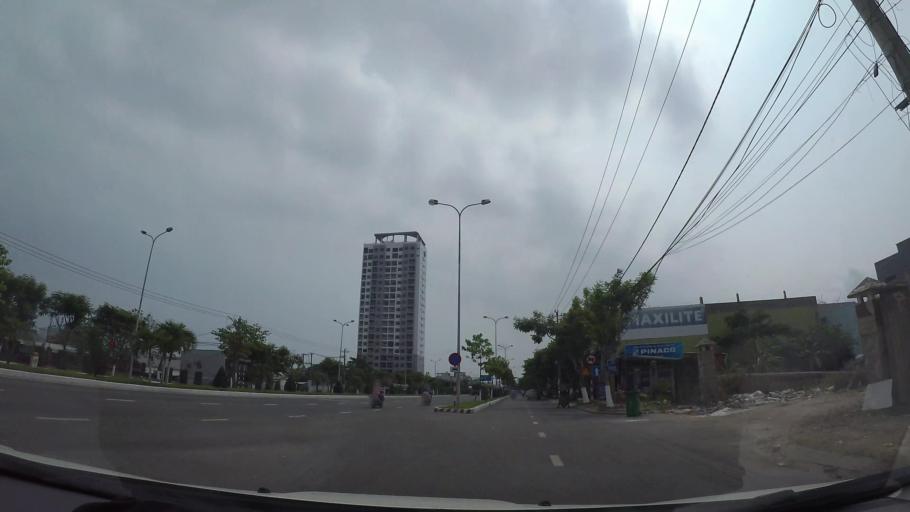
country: VN
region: Da Nang
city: Da Nang
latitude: 16.0980
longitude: 108.2459
